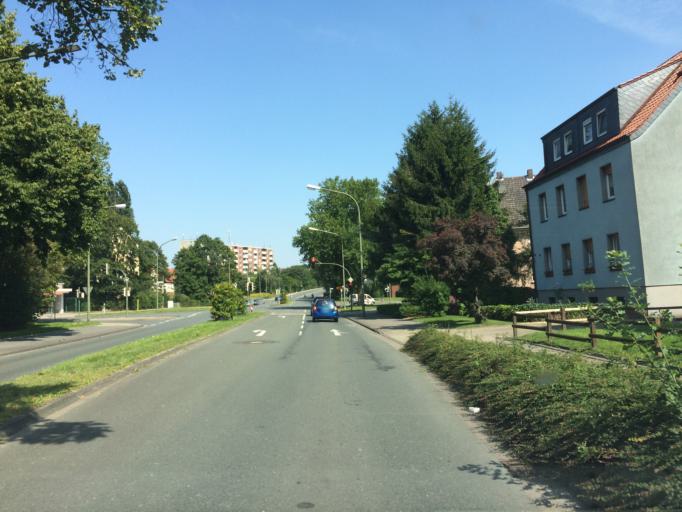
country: DE
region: North Rhine-Westphalia
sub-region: Regierungsbezirk Arnsberg
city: Hamm
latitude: 51.6678
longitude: 7.7719
